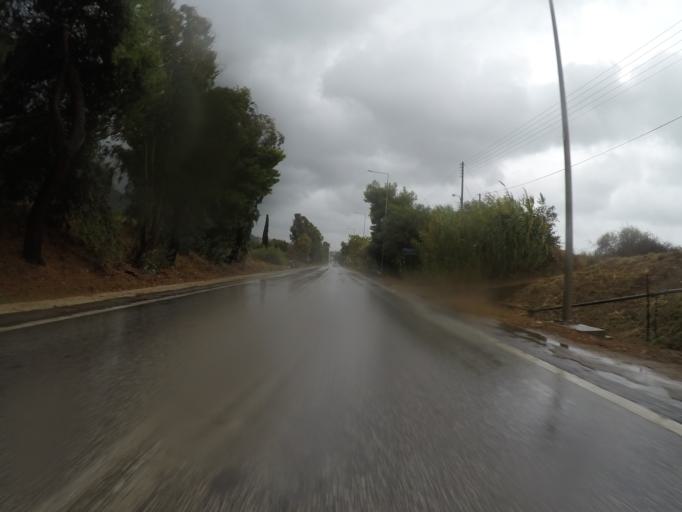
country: GR
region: Peloponnese
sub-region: Nomos Messinias
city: Kyparissia
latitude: 37.2587
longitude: 21.6828
